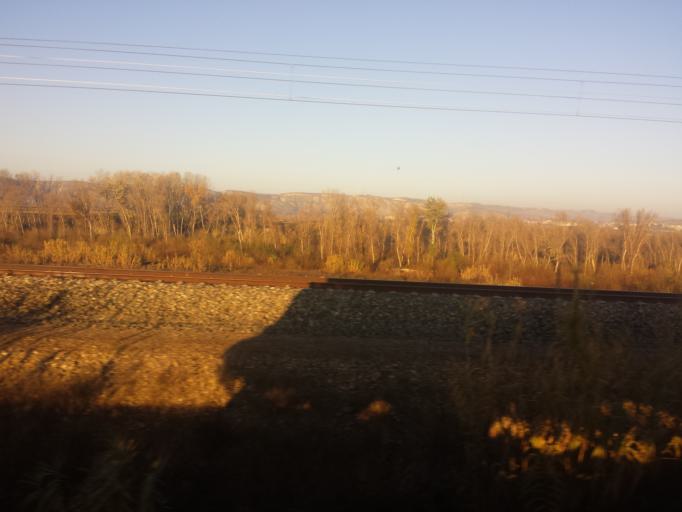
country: ES
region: Aragon
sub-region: Provincia de Zaragoza
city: Zuera
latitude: 41.8497
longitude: -0.7781
